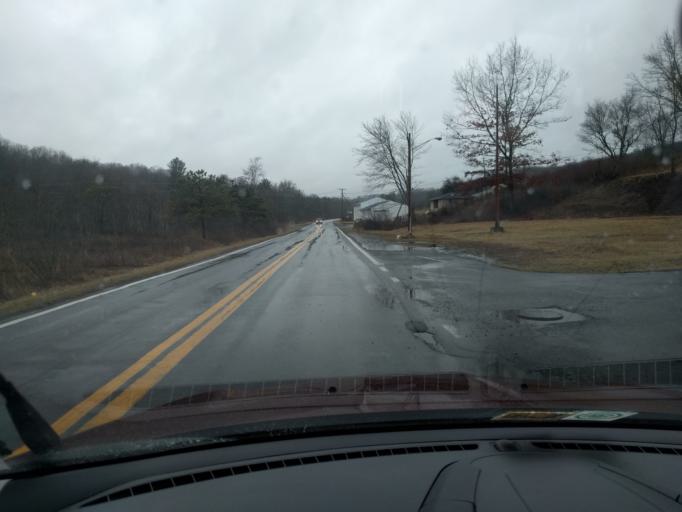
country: US
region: West Virginia
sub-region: Raleigh County
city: Beckley
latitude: 37.7911
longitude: -81.1902
